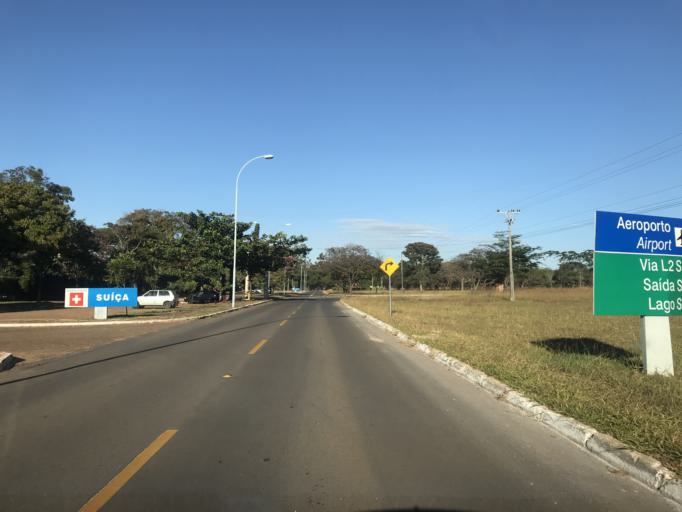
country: BR
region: Federal District
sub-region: Brasilia
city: Brasilia
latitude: -15.8305
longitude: -47.8982
